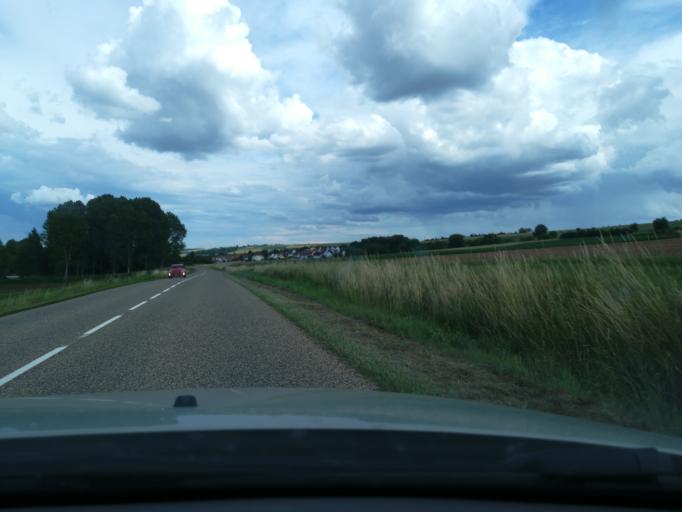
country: FR
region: Alsace
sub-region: Departement du Bas-Rhin
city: Obermodern-Zutzendorf
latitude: 48.8508
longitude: 7.5196
